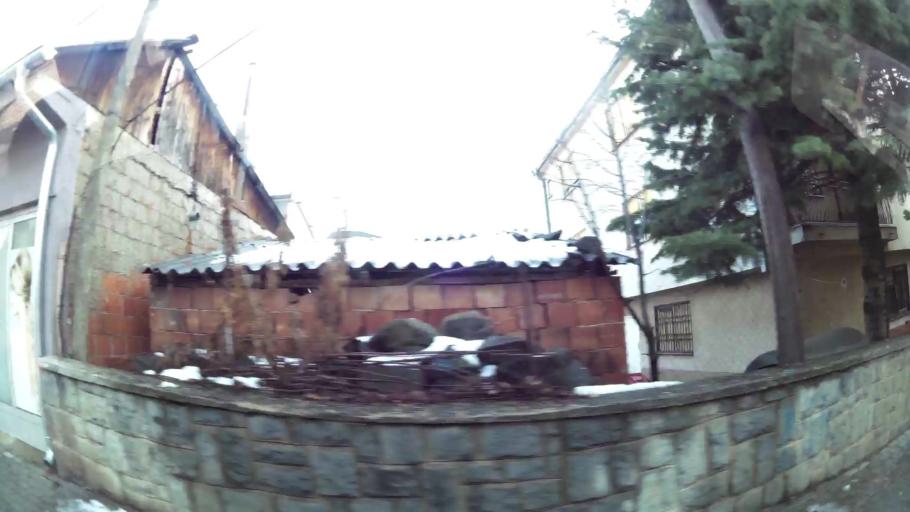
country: XK
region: Pristina
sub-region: Komuna e Prishtines
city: Pristina
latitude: 42.6692
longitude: 21.1739
